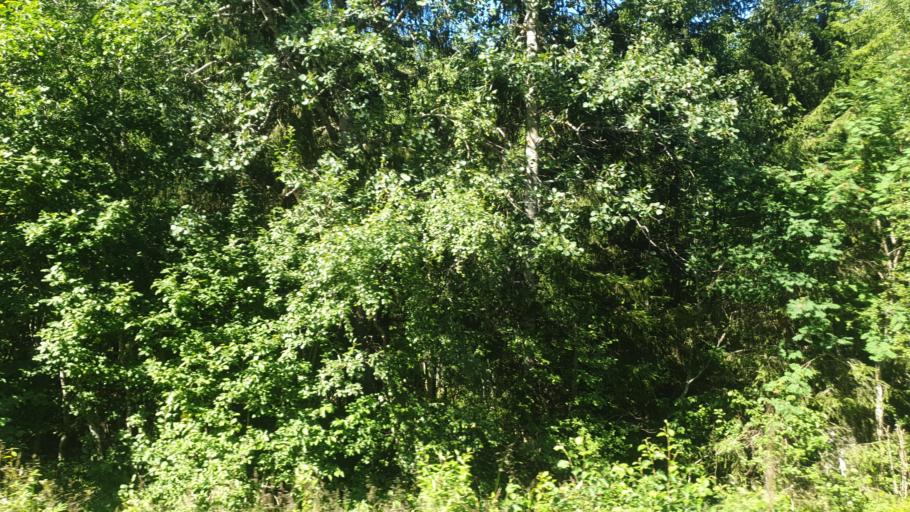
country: NO
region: Sor-Trondelag
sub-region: Meldal
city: Meldal
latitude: 63.1423
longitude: 9.7123
